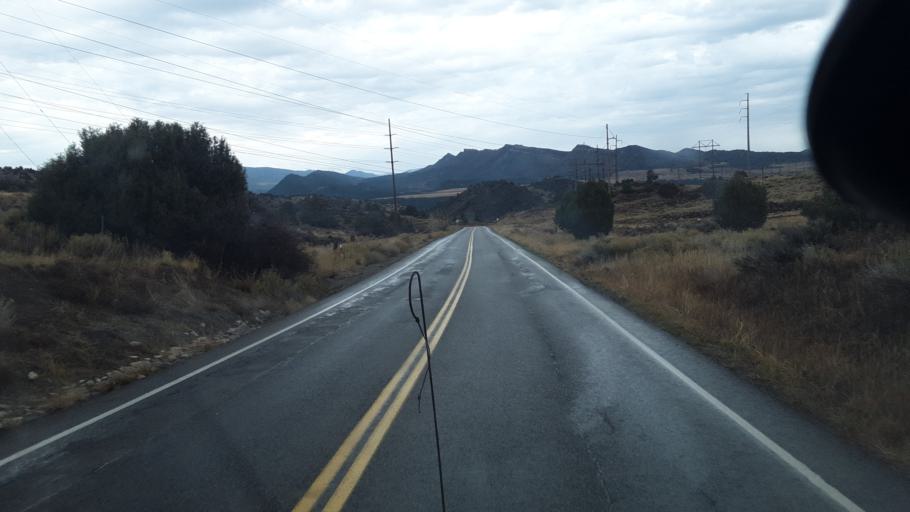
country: US
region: Colorado
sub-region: La Plata County
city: Durango
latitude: 37.2429
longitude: -107.8988
